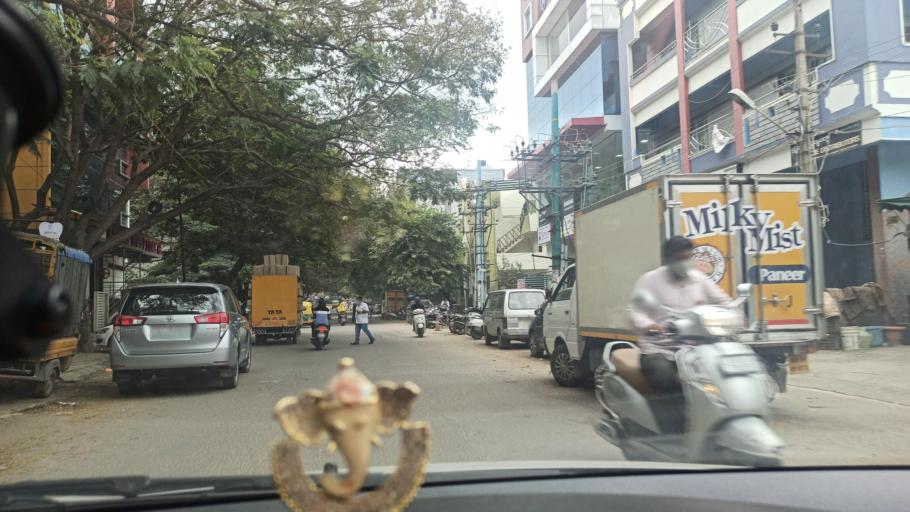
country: IN
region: Karnataka
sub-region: Bangalore Urban
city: Bangalore
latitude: 12.9151
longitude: 77.6490
